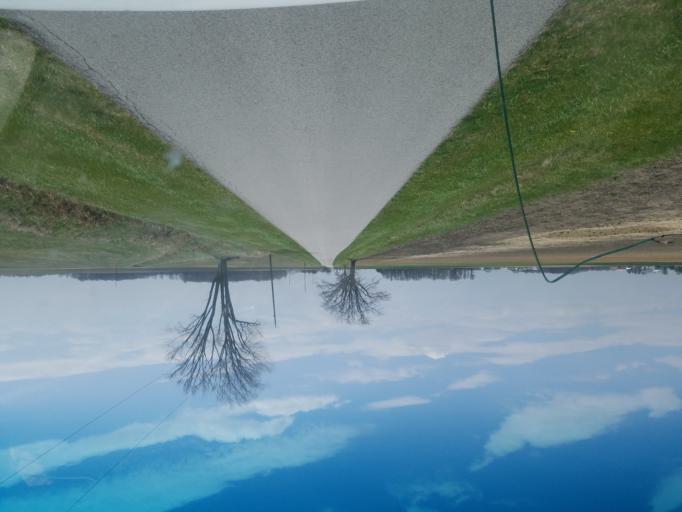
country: US
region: Ohio
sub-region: Hardin County
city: Forest
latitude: 40.7743
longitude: -83.4806
